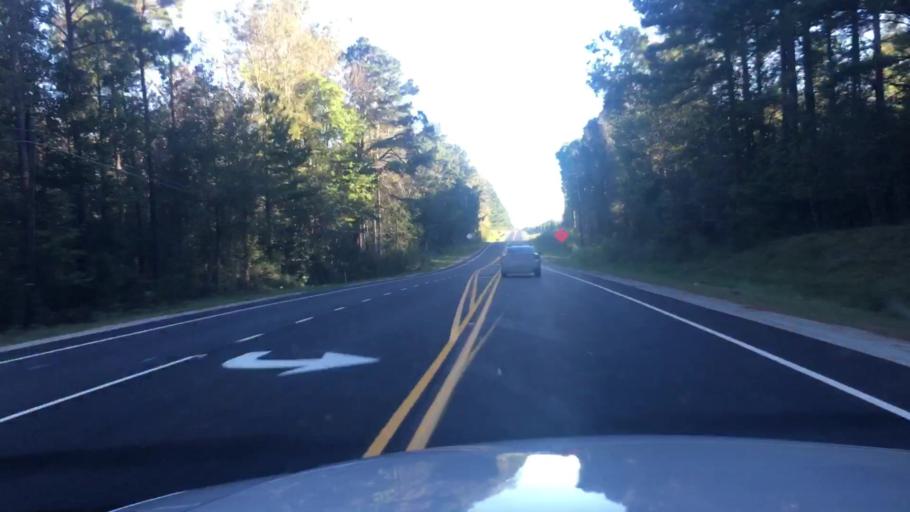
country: US
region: North Carolina
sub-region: Harnett County
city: Walkertown
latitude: 35.3415
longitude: -78.8552
